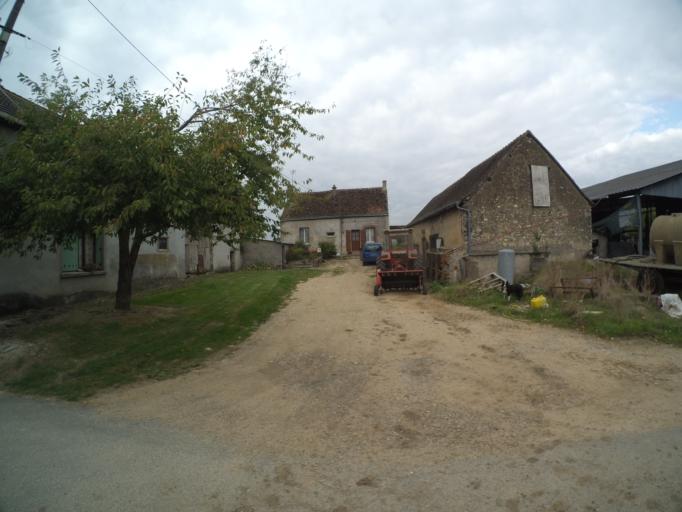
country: FR
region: Centre
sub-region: Departement d'Indre-et-Loire
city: Auzouer-en-Touraine
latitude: 47.5093
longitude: 0.9425
